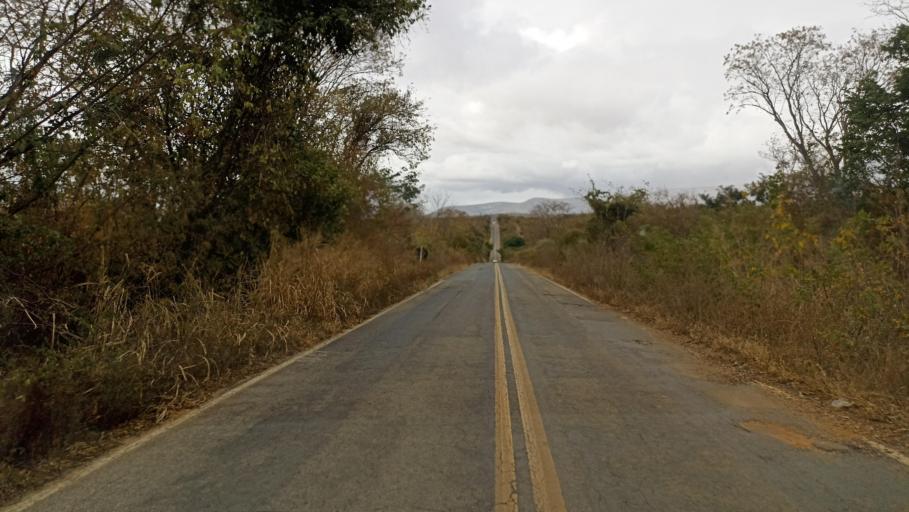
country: BR
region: Minas Gerais
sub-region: Itinga
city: Itinga
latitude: -16.6411
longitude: -41.8178
